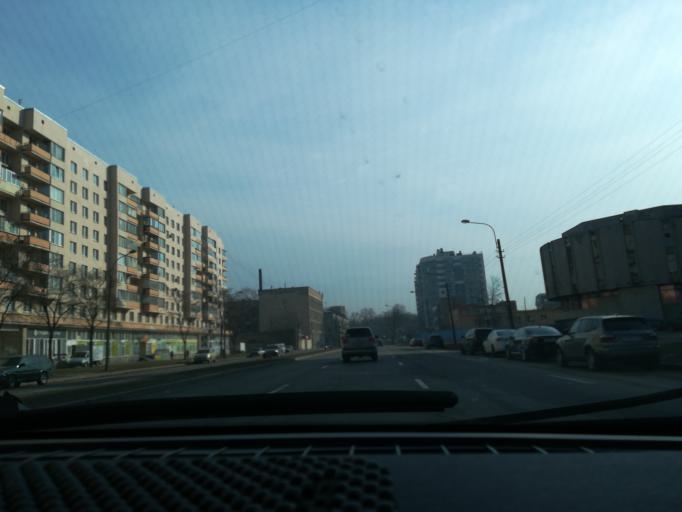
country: RU
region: St.-Petersburg
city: Vasyl'evsky Ostrov
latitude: 59.9489
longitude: 30.2442
